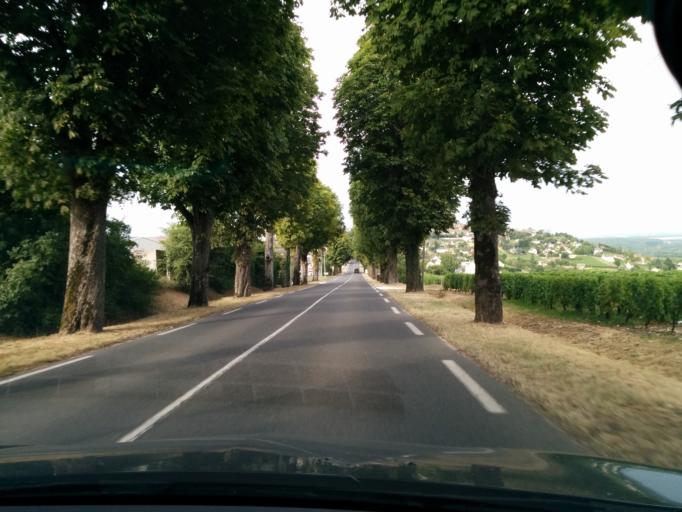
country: FR
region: Centre
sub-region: Departement du Cher
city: Sancerre
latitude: 47.3239
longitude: 2.8227
